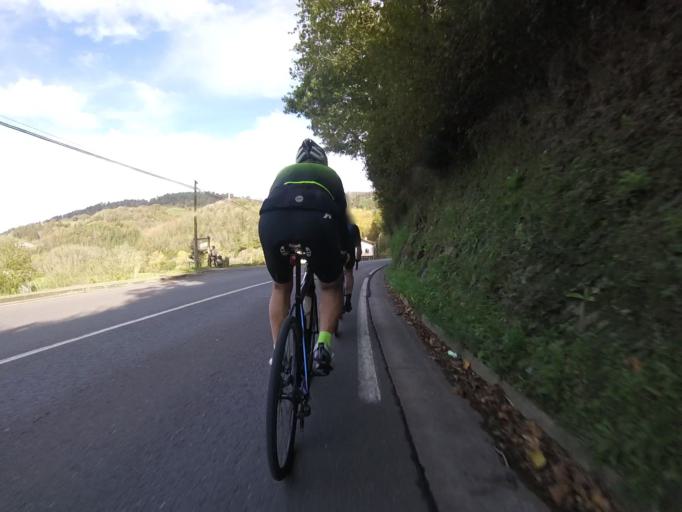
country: ES
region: Basque Country
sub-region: Provincia de Guipuzcoa
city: Usurbil
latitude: 43.2799
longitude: -2.0729
